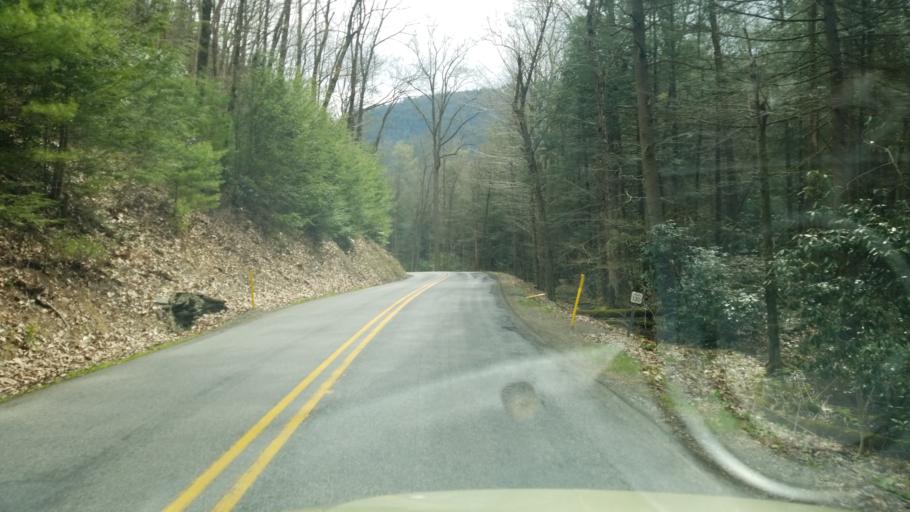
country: US
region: Pennsylvania
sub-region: Cameron County
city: Emporium
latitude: 41.2828
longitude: -78.1328
